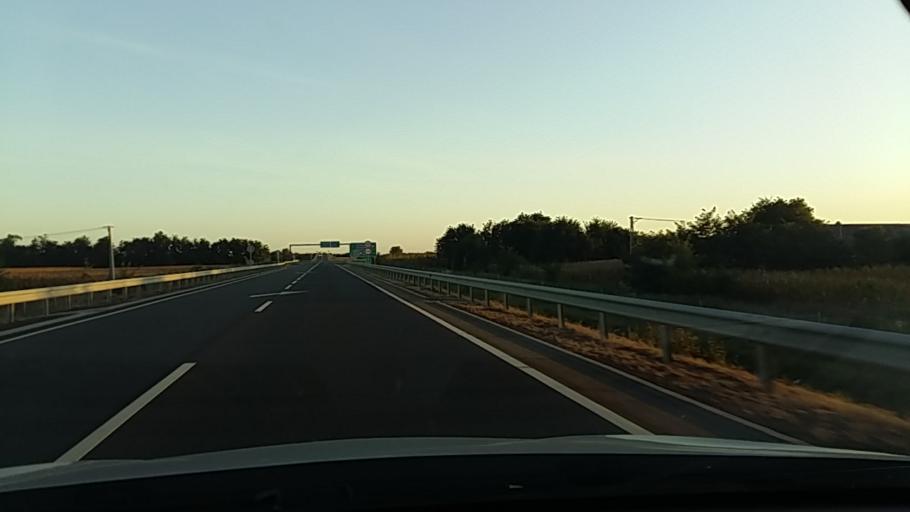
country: HU
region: Szabolcs-Szatmar-Bereg
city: Kalmanhaza
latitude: 47.9079
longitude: 21.6433
